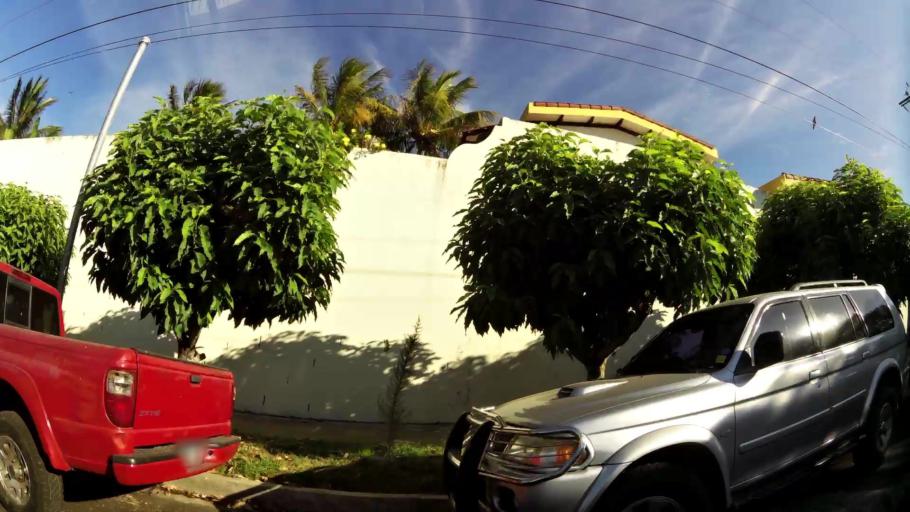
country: SV
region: La Libertad
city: Santa Tecla
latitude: 13.6847
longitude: -89.2892
